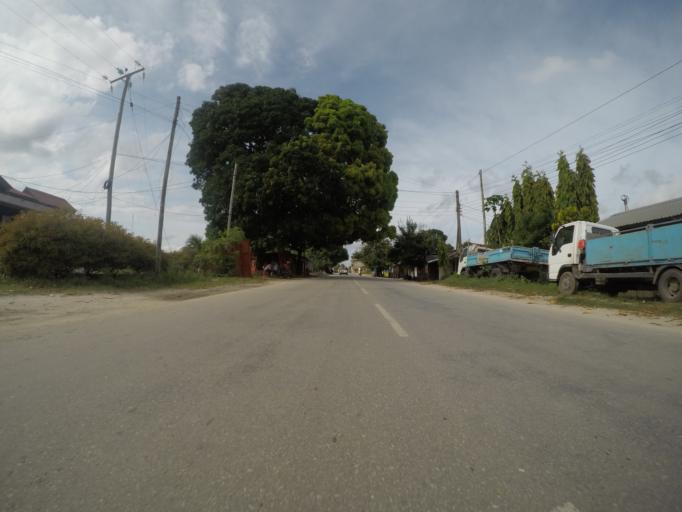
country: TZ
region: Pemba South
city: Chake Chake
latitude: -5.2281
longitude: 39.7755
